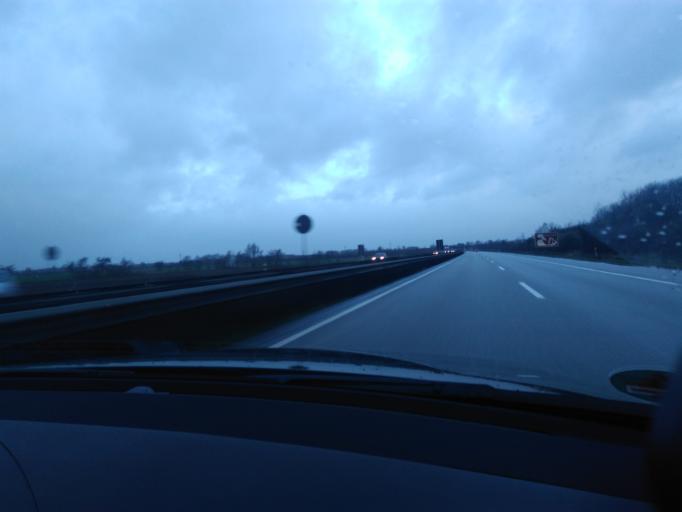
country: DE
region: Schleswig-Holstein
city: Padenstedt
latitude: 54.0254
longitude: 9.9323
